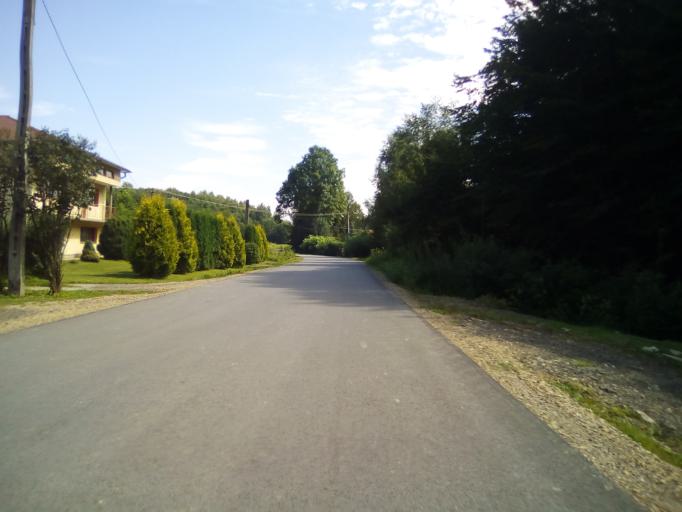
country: PL
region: Subcarpathian Voivodeship
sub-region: Powiat brzozowski
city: Domaradz
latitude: 49.8092
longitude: 21.9272
